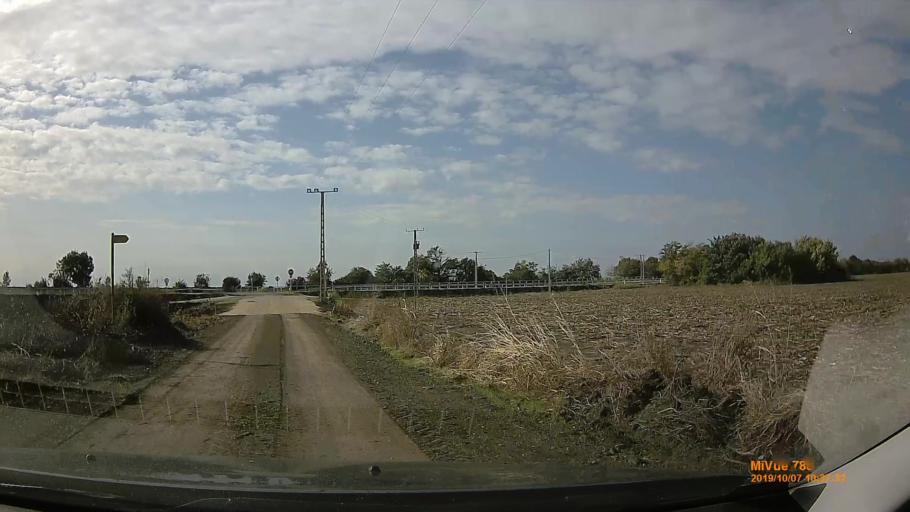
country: HU
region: Bekes
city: Kondoros
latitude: 46.7487
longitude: 20.8478
